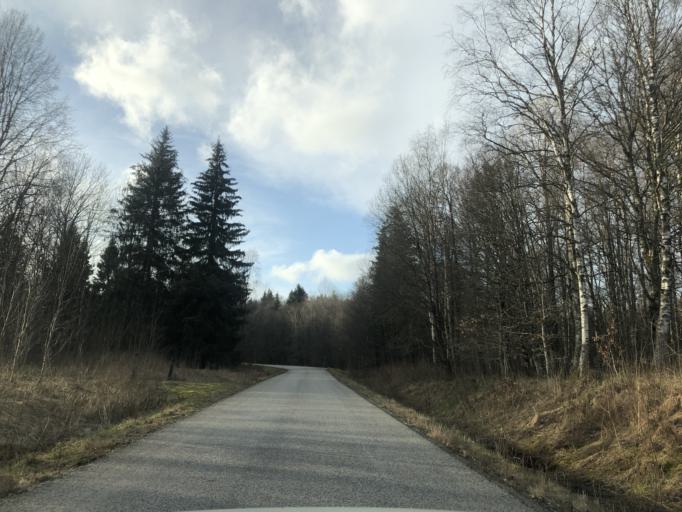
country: SE
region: Vaestra Goetaland
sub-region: Ulricehamns Kommun
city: Ulricehamn
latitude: 57.8035
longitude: 13.3720
